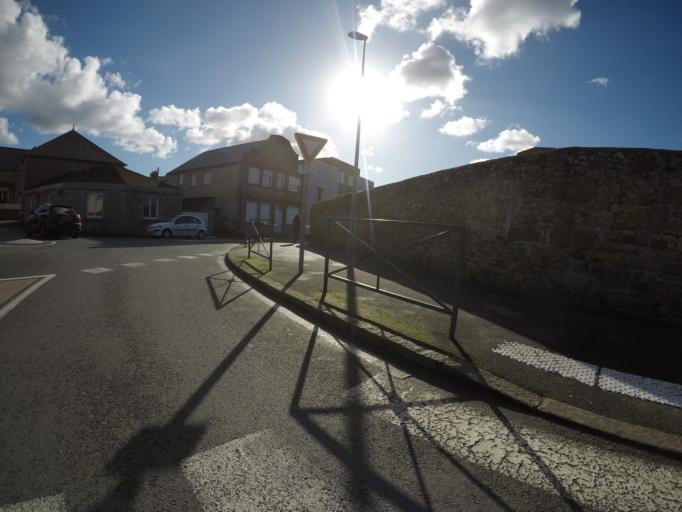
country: FR
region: Brittany
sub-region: Departement des Cotes-d'Armor
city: Guingamp
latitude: 48.5614
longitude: -3.1440
